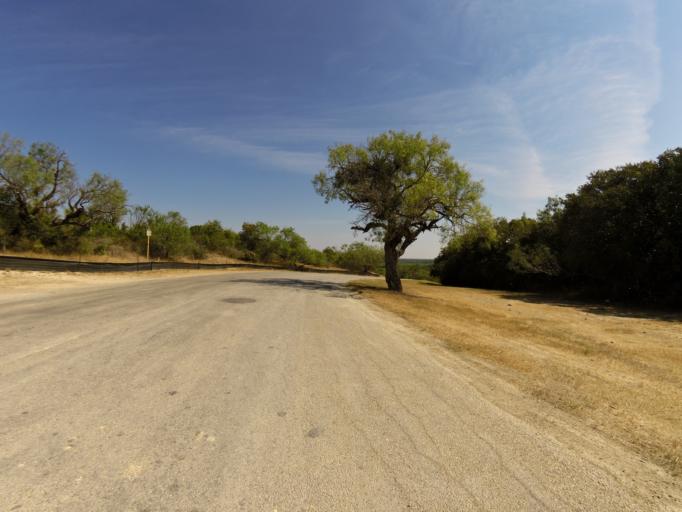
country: US
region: Texas
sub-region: Bexar County
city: San Antonio
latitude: 29.3838
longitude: -98.4349
